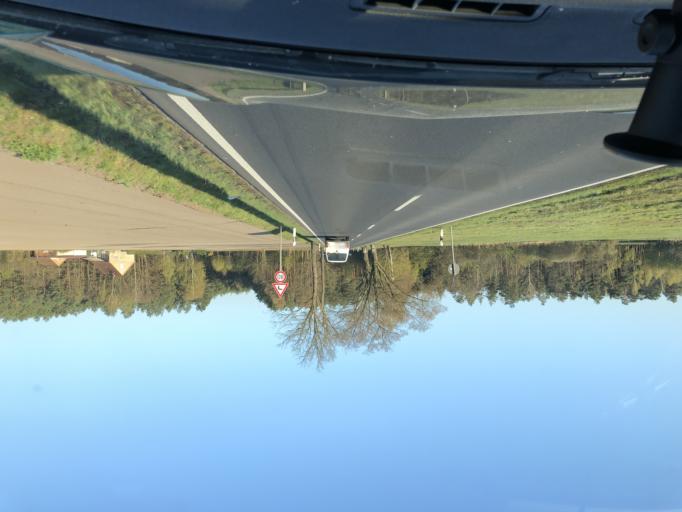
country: DE
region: Saxony
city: Krauschwitz
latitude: 51.5079
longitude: 14.7159
